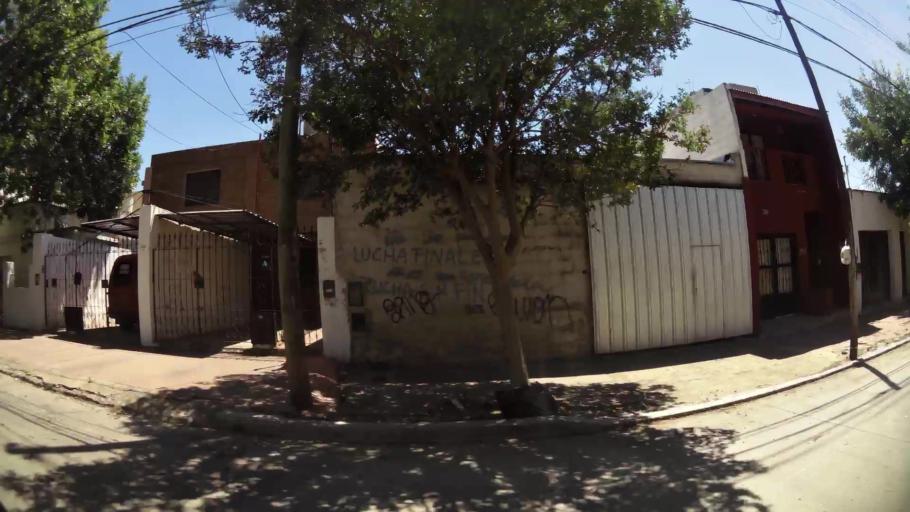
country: AR
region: Cordoba
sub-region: Departamento de Capital
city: Cordoba
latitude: -31.4084
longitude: -64.2123
